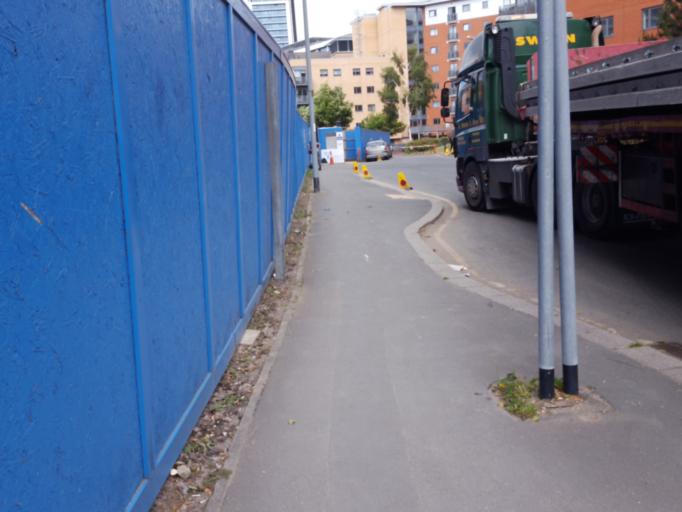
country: GB
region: England
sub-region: City and Borough of Leeds
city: Leeds
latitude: 53.7887
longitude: -1.5485
